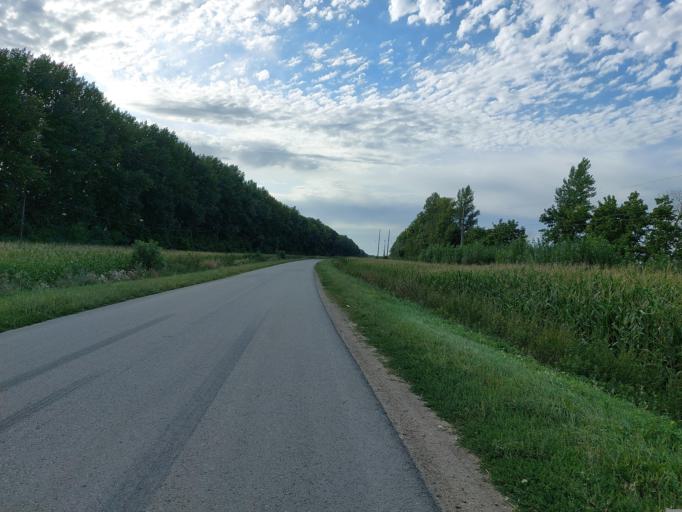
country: RU
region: Lipetsk
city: Dolgorukovo
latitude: 52.3157
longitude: 38.1593
